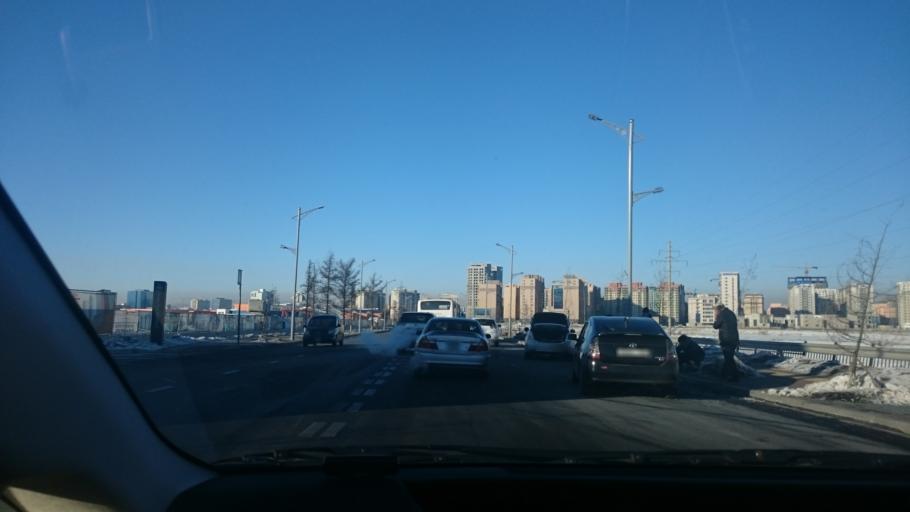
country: MN
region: Ulaanbaatar
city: Ulaanbaatar
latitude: 47.8954
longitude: 106.9346
